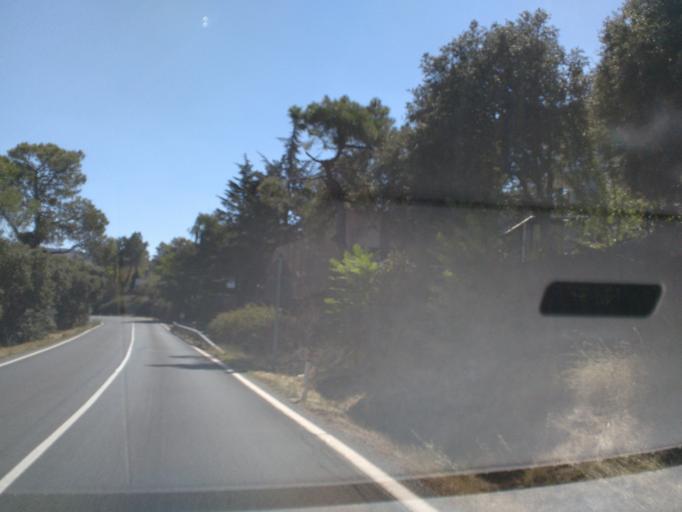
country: ES
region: Madrid
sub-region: Provincia de Madrid
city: Robledo de Chavela
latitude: 40.5164
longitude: -4.2461
